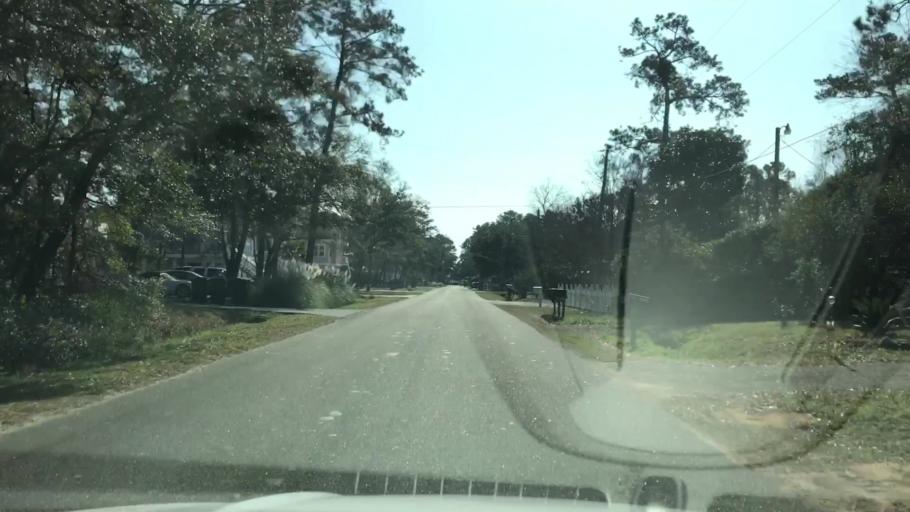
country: US
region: South Carolina
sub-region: Horry County
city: Garden City
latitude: 33.5859
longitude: -79.0042
